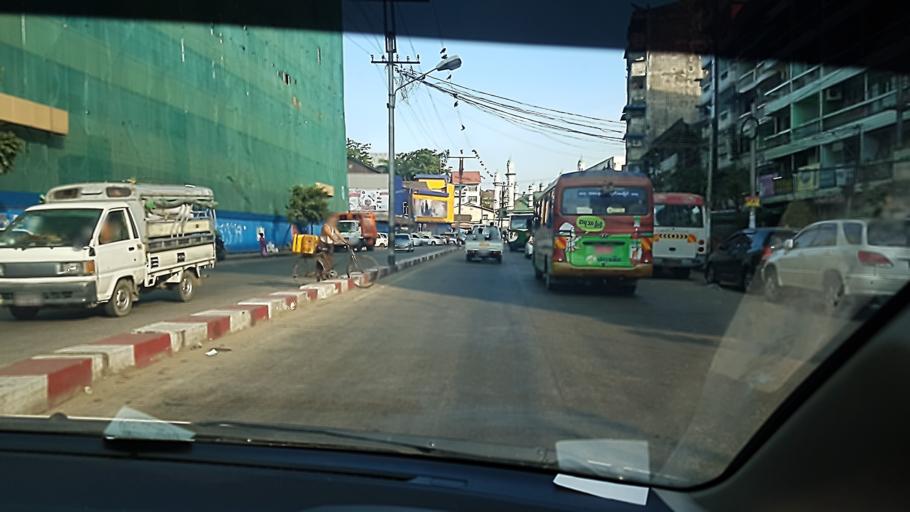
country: MM
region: Yangon
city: Yangon
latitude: 16.8108
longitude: 96.1751
